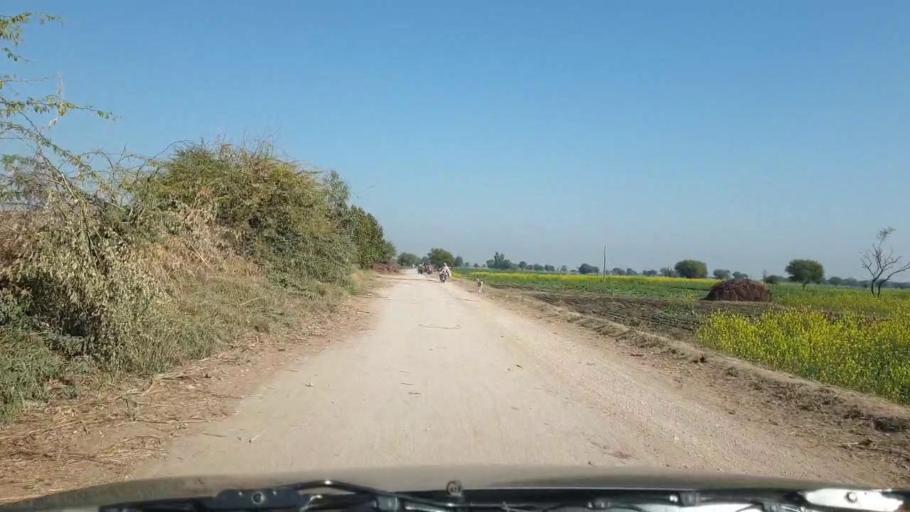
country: PK
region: Sindh
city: Jhol
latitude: 25.9498
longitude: 68.8200
